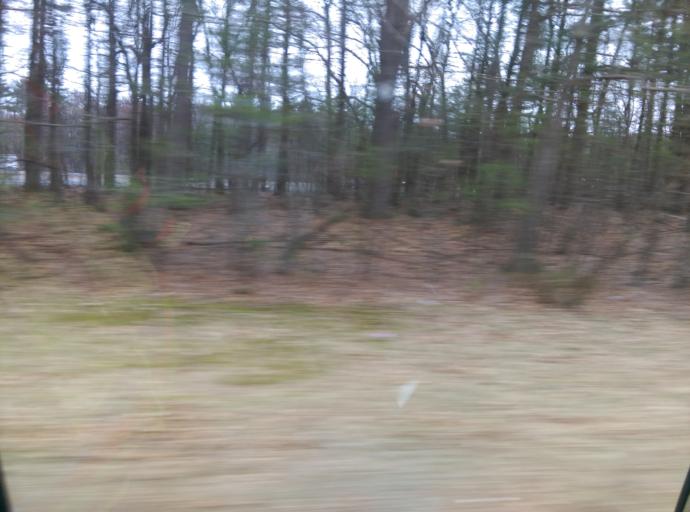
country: US
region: New Hampshire
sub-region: Rockingham County
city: Seabrook
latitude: 42.8765
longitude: -70.8865
